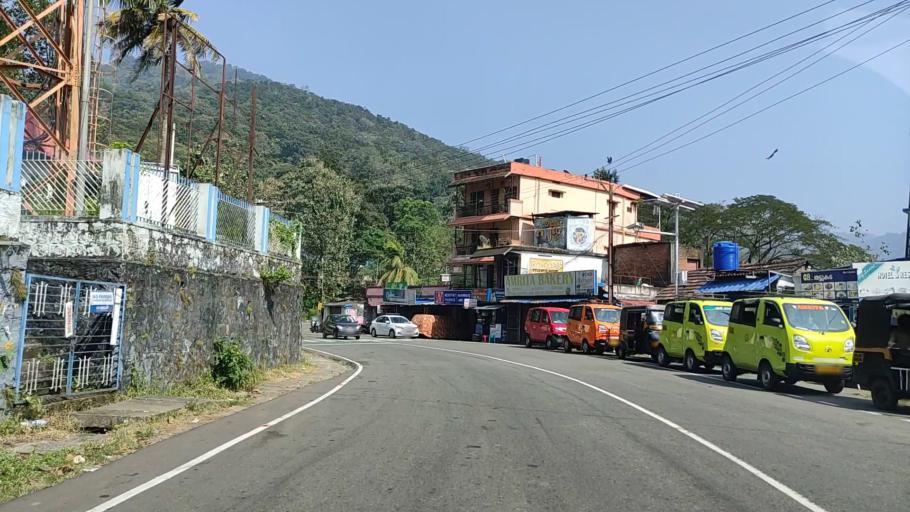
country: IN
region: Kerala
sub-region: Kollam
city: Punalur
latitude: 8.9678
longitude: 77.0703
